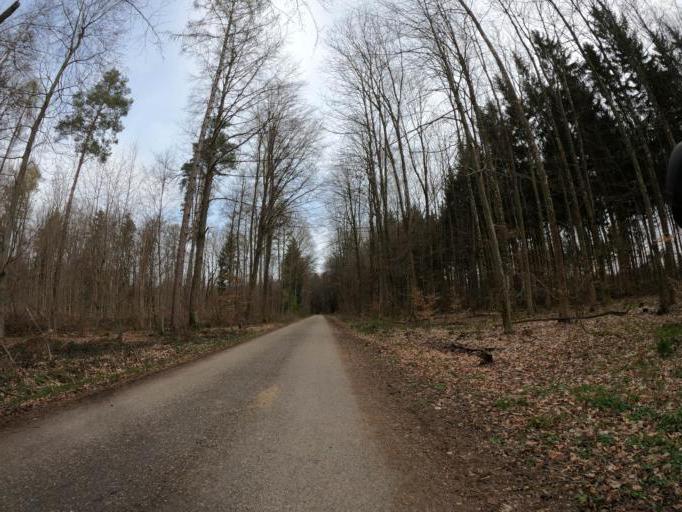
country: DE
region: Baden-Wuerttemberg
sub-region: Regierungsbezirk Stuttgart
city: Waldenbuch
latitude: 48.6148
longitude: 9.1340
